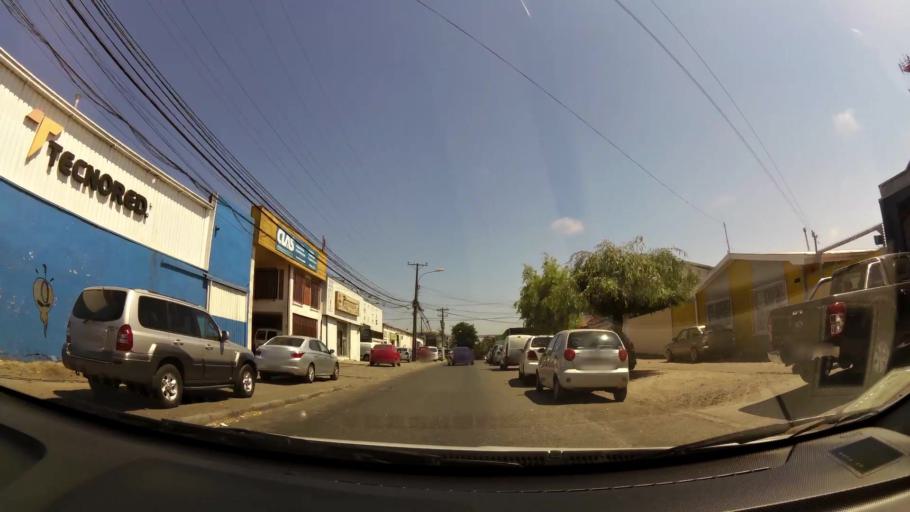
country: CL
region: Biobio
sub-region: Provincia de Concepcion
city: Concepcion
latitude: -36.8064
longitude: -73.0517
